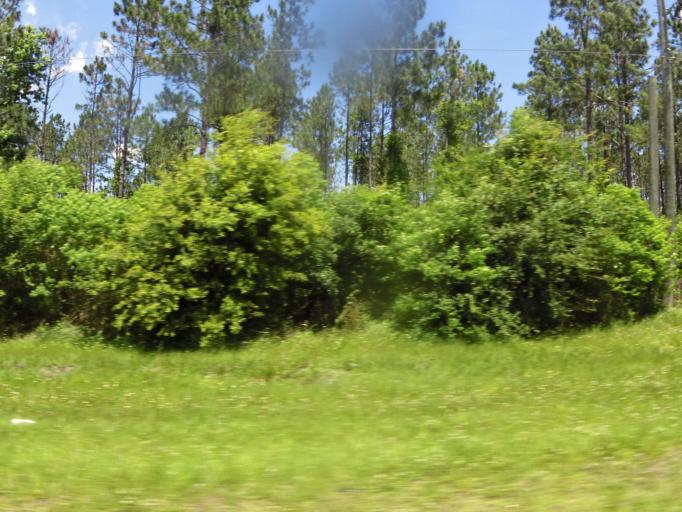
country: US
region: Florida
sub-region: Bradford County
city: Starke
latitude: 30.0413
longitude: -82.1564
